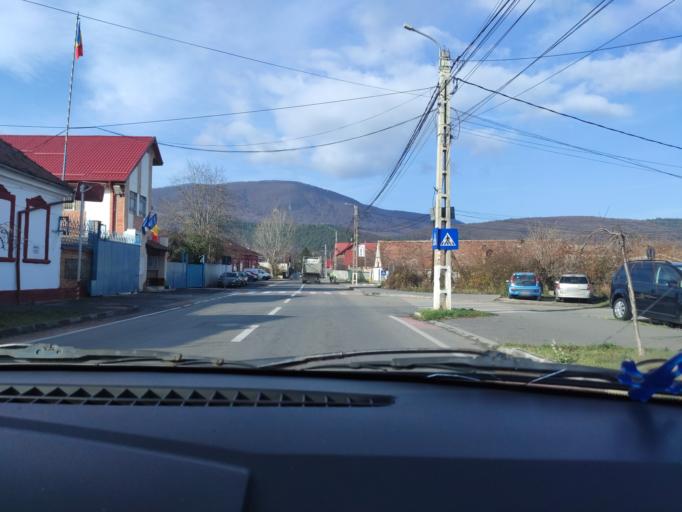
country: RO
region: Brasov
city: Codlea
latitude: 45.6952
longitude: 25.4535
